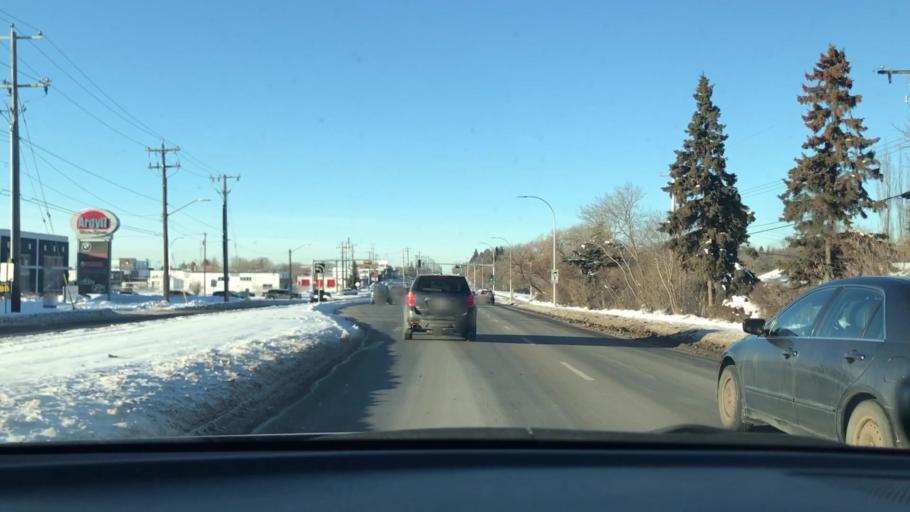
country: CA
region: Alberta
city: Edmonton
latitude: 53.5000
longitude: -113.4649
